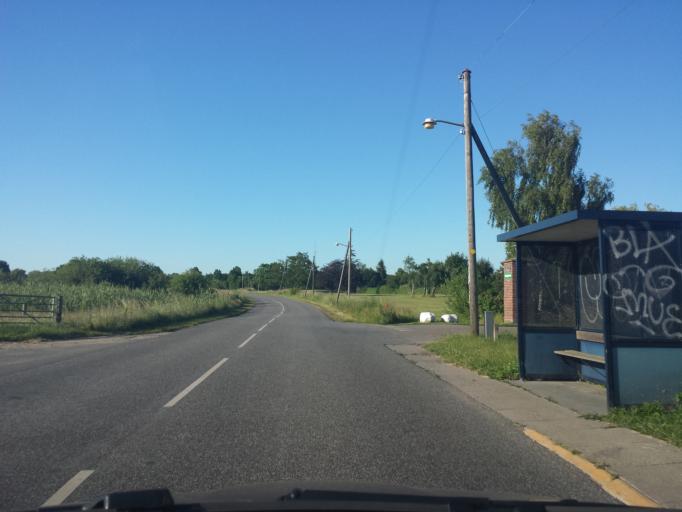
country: DK
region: Capital Region
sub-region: Ballerup Kommune
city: Ballerup
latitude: 55.7053
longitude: 12.3757
